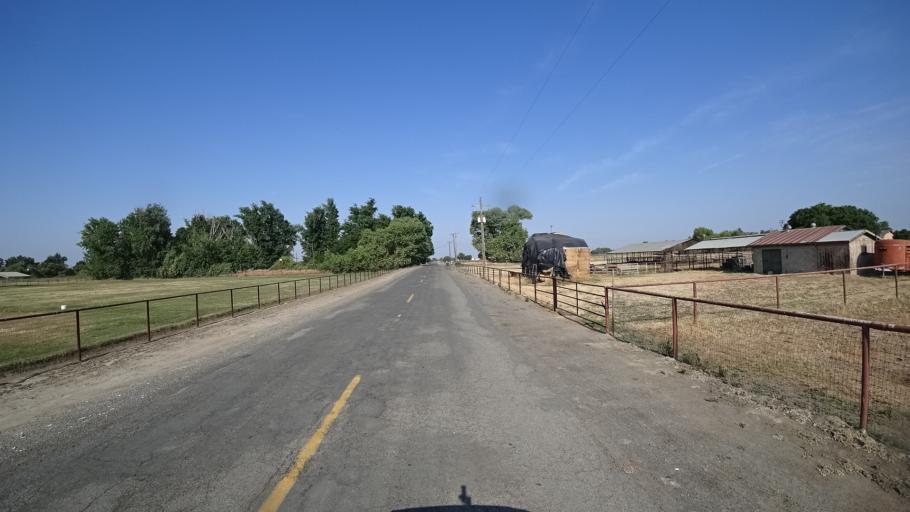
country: US
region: California
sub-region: Fresno County
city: Riverdale
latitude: 36.3731
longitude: -119.8195
